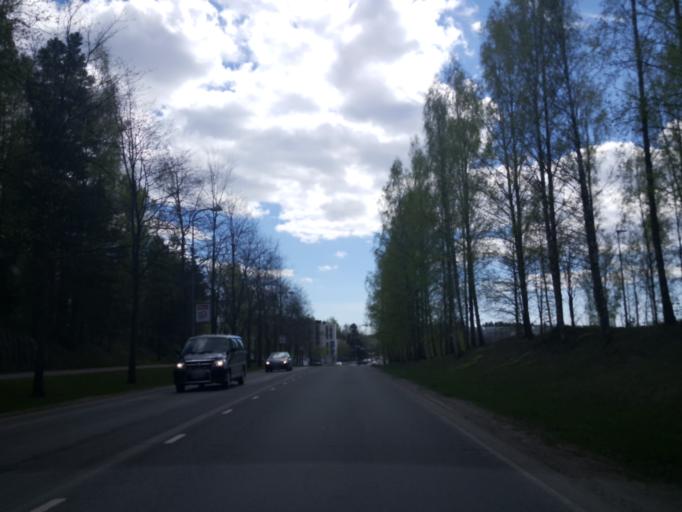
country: FI
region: Uusimaa
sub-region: Helsinki
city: Teekkarikylae
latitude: 60.2658
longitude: 24.8425
